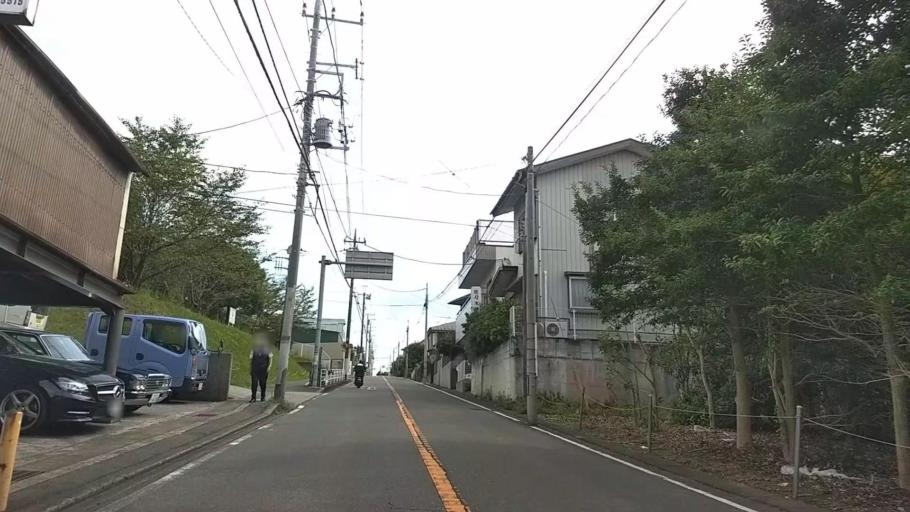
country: JP
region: Kanagawa
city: Yokohama
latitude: 35.4991
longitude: 139.5827
